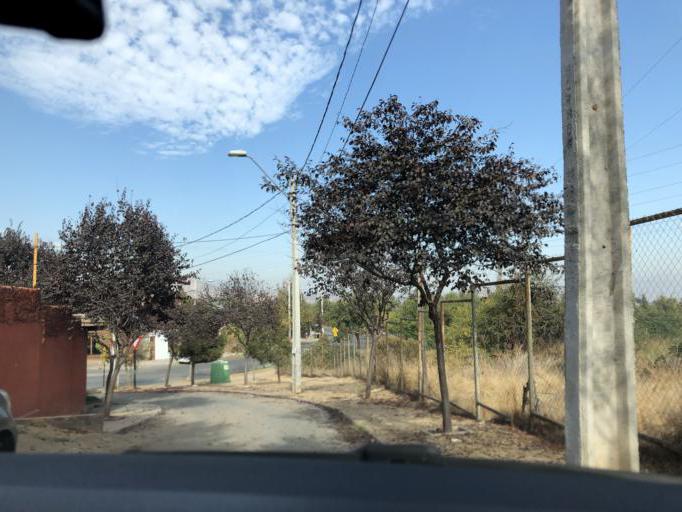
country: CL
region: Santiago Metropolitan
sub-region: Provincia de Cordillera
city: Puente Alto
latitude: -33.5889
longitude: -70.5378
